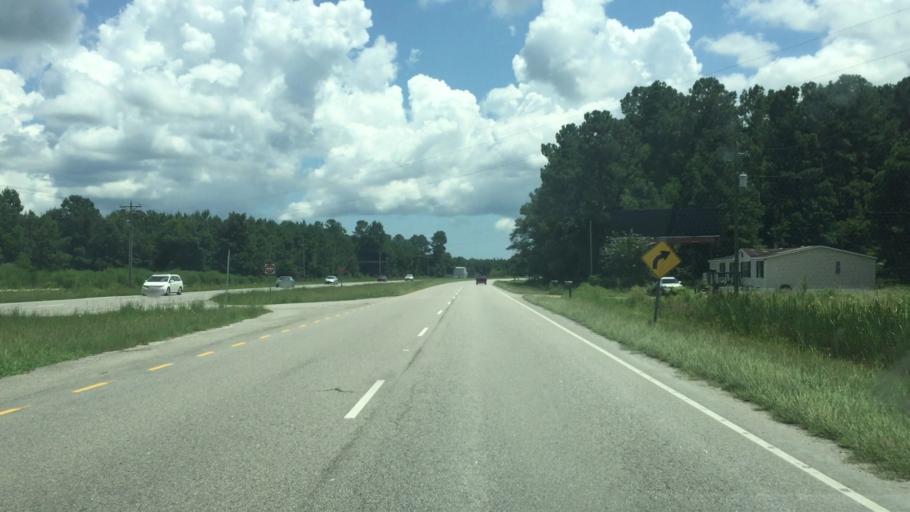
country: US
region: South Carolina
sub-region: Horry County
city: Loris
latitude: 34.0022
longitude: -78.7569
